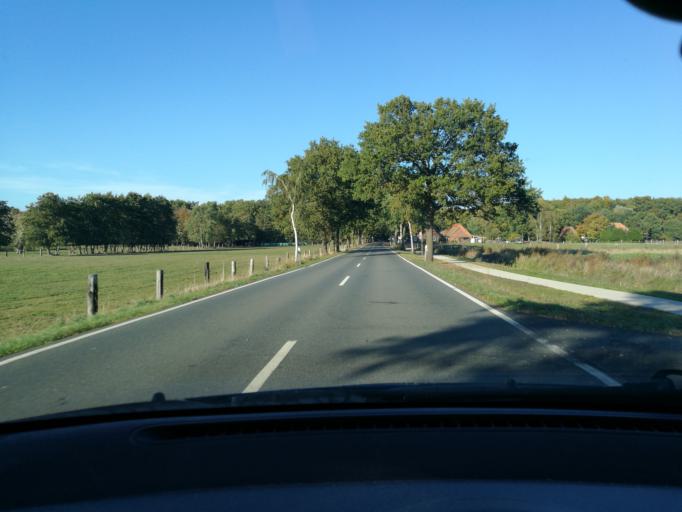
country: DE
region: Lower Saxony
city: Rullstorf
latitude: 53.2943
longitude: 10.5580
